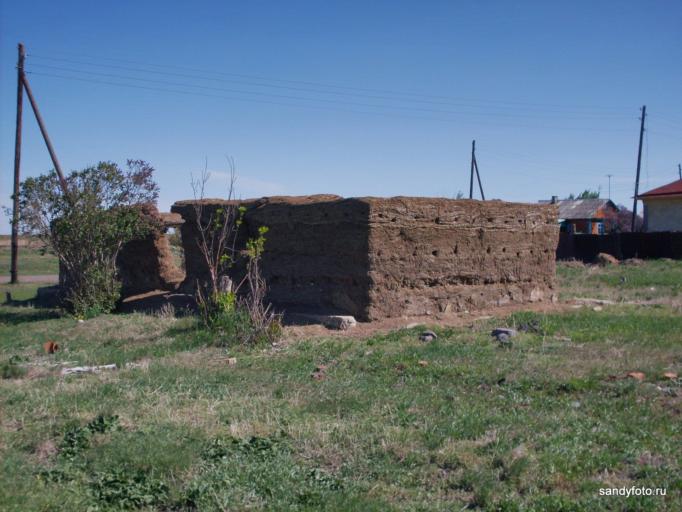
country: RU
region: Chelyabinsk
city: Bobrovka
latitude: 54.1599
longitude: 61.8146
